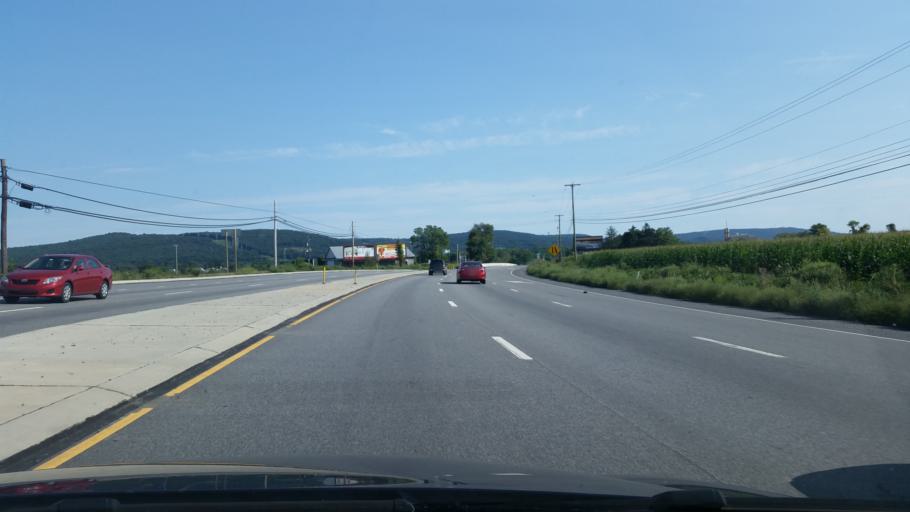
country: US
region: Pennsylvania
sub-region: Berks County
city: Leesport
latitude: 40.4392
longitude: -75.9450
